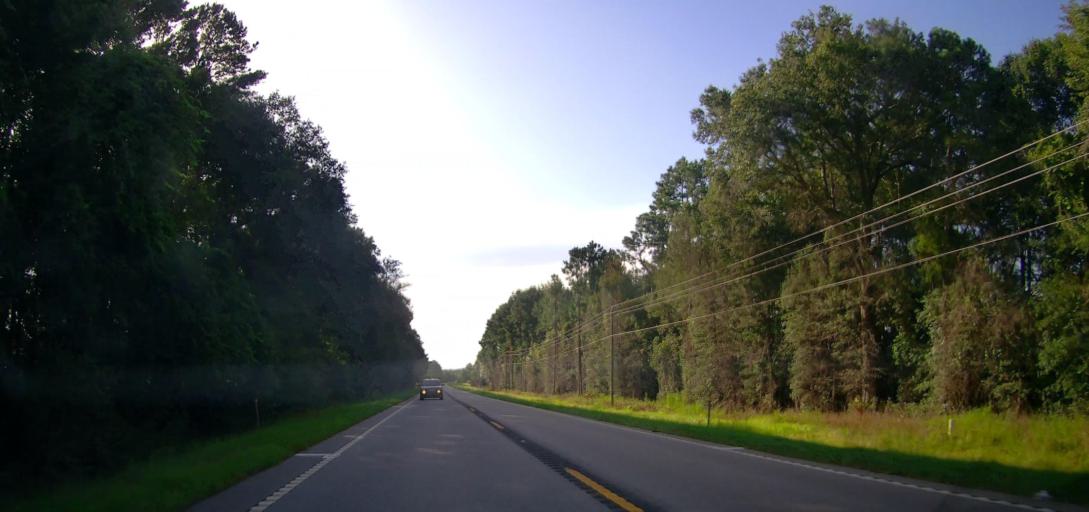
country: US
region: Georgia
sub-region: Coffee County
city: Nicholls
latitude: 31.3898
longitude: -82.6575
